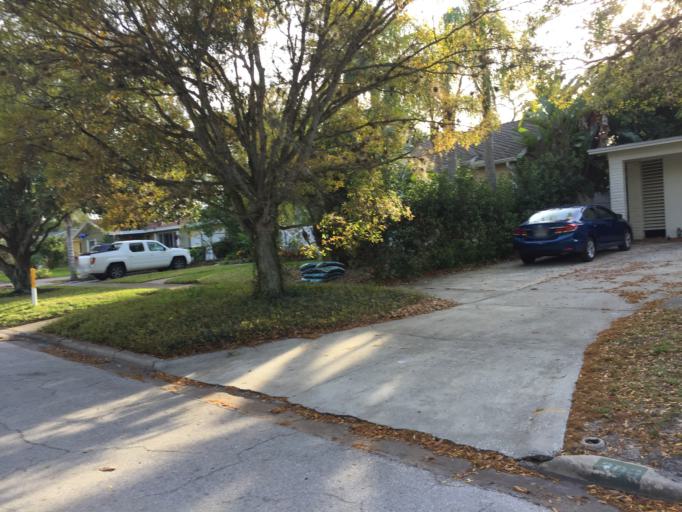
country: US
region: Florida
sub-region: Pinellas County
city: Clearwater
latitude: 27.9697
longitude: -82.7744
